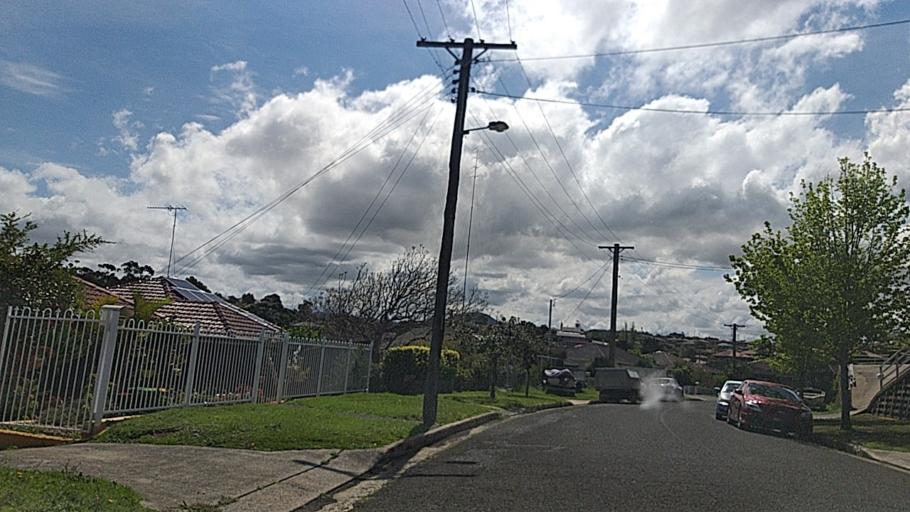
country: AU
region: New South Wales
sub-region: Wollongong
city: Lake Heights
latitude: -34.4891
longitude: 150.8771
